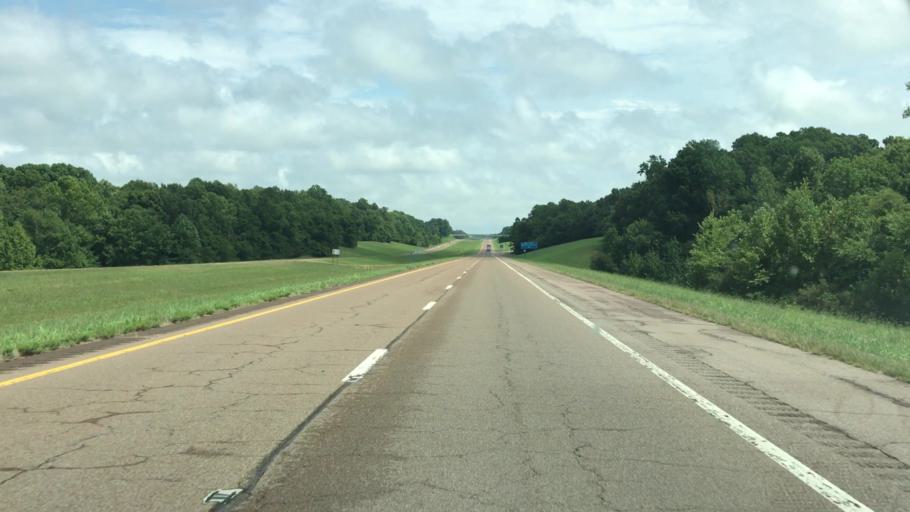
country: US
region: Tennessee
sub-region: Dyer County
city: Dyersburg
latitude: 36.0733
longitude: -89.4797
